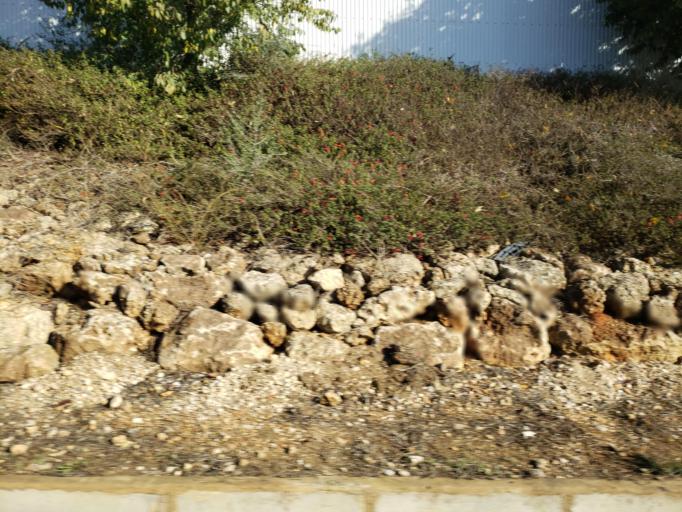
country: PT
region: Faro
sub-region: Portimao
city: Portimao
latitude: 37.1524
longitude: -8.5583
